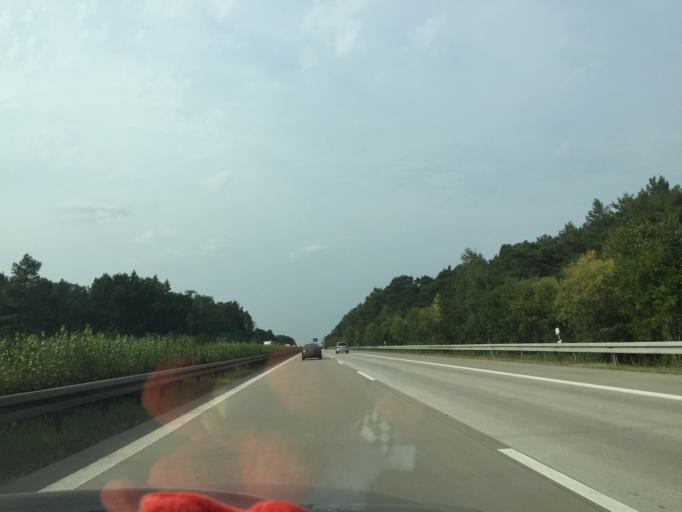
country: DE
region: Brandenburg
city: Bestensee
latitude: 52.2332
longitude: 13.5935
